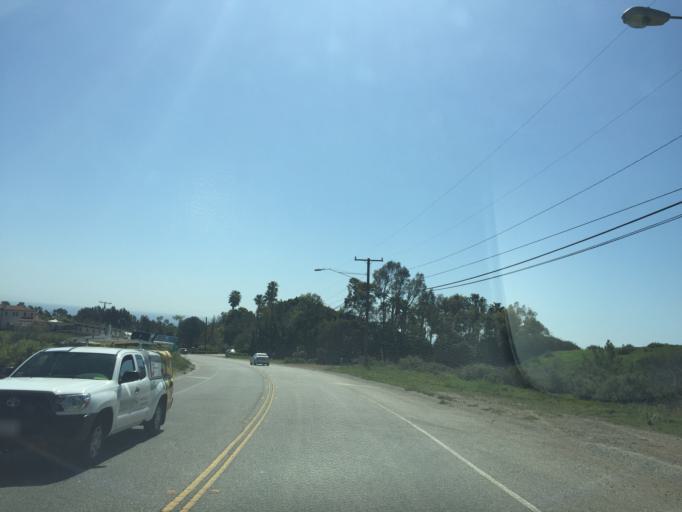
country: US
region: California
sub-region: Los Angeles County
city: Malibu
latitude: 34.0350
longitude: -118.8004
